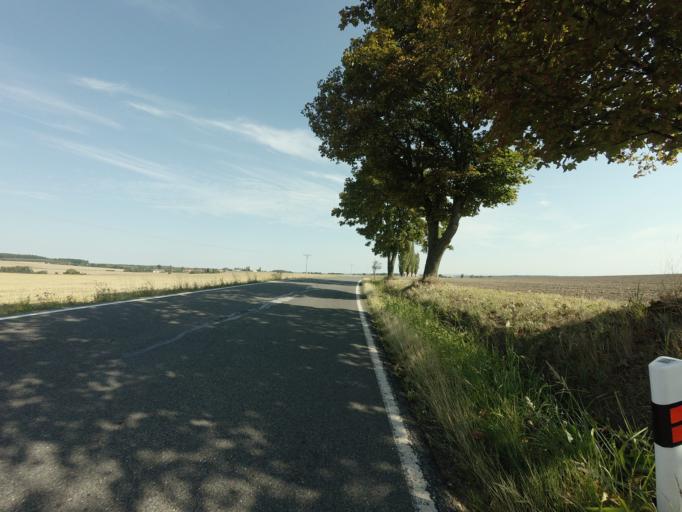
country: CZ
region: Jihocesky
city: Bernartice
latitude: 49.3305
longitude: 14.3599
